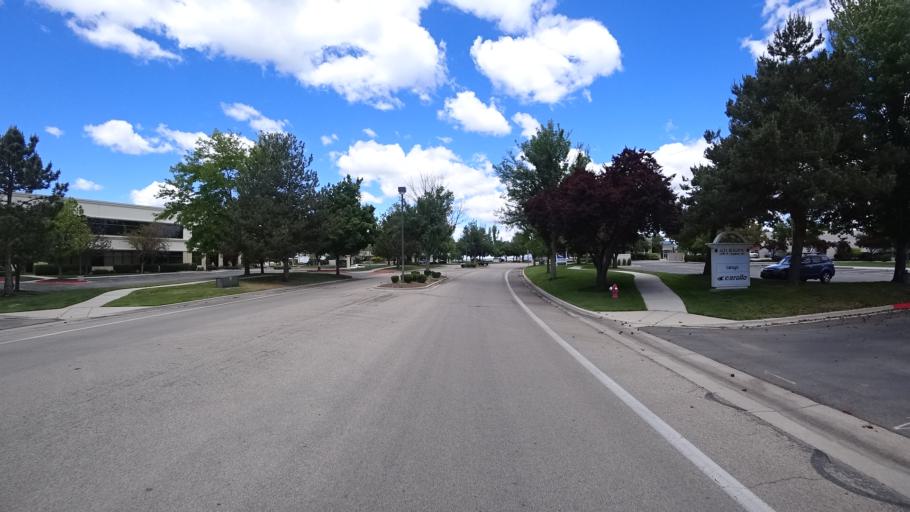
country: US
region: Idaho
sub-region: Ada County
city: Eagle
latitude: 43.6611
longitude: -116.3389
